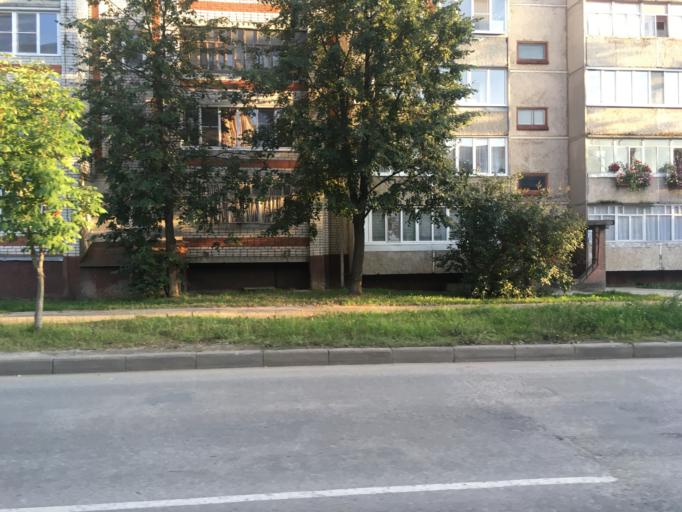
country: RU
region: Mariy-El
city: Yoshkar-Ola
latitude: 56.6507
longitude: 47.8736
